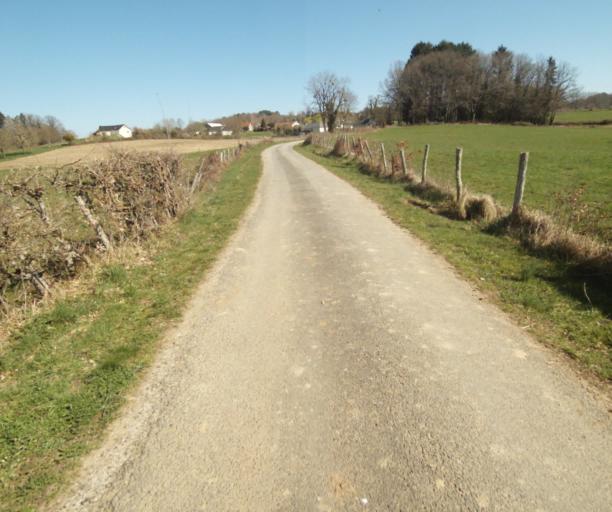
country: FR
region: Limousin
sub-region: Departement de la Correze
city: Saint-Mexant
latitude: 45.3045
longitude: 1.6006
